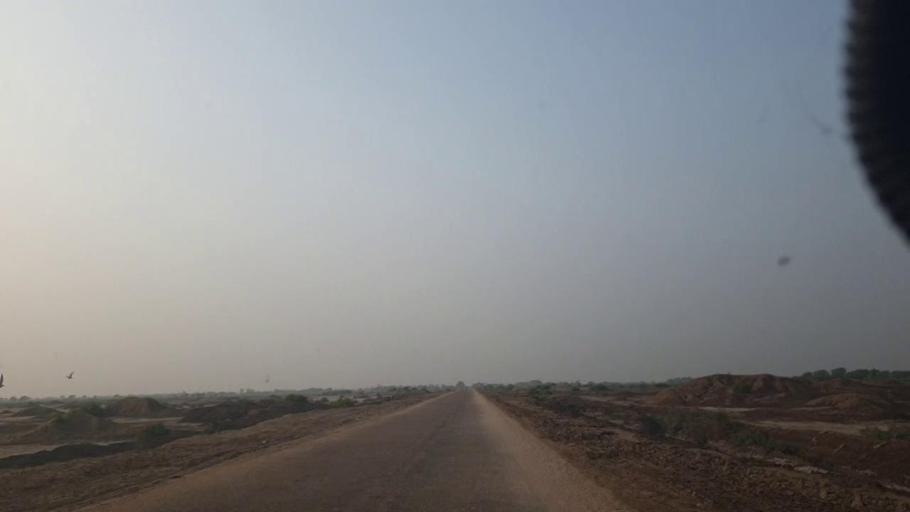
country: PK
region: Sindh
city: Bulri
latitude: 24.8550
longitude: 68.4027
